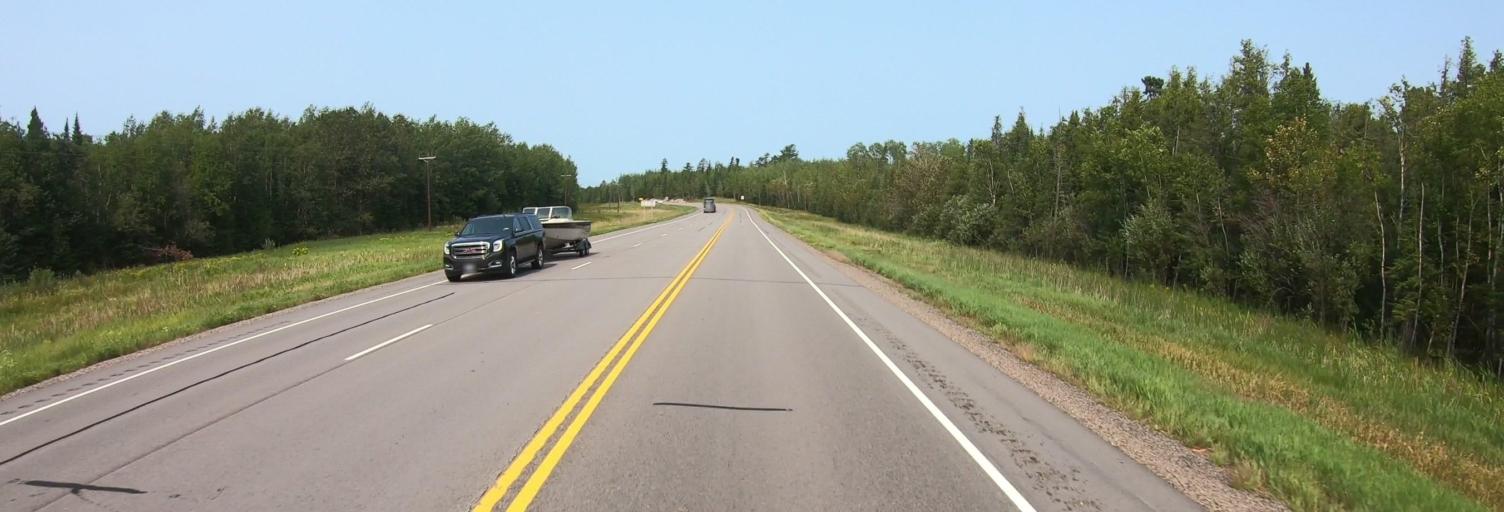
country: CA
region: Ontario
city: Fort Frances
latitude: 48.3992
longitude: -93.0160
